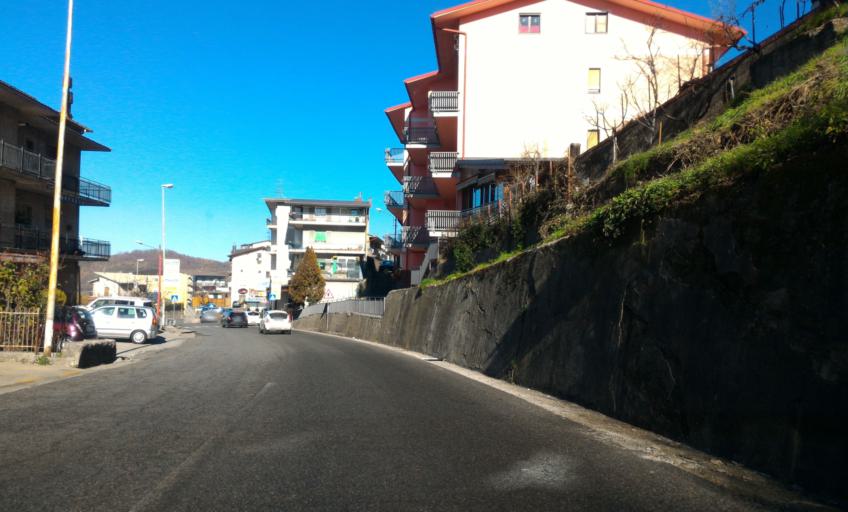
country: IT
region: Calabria
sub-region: Provincia di Cosenza
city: Spezzano della Sila
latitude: 39.3024
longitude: 16.3405
